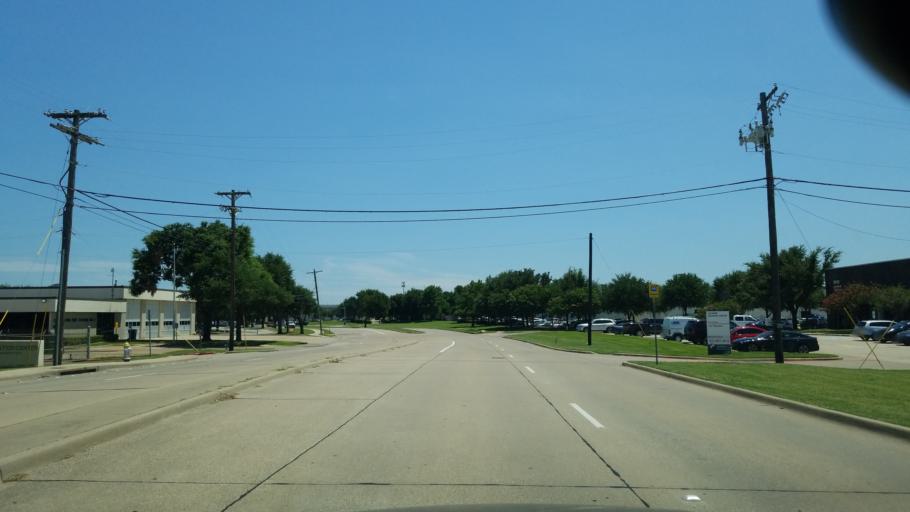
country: US
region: Texas
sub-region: Dallas County
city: Farmers Branch
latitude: 32.9413
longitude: -96.9167
